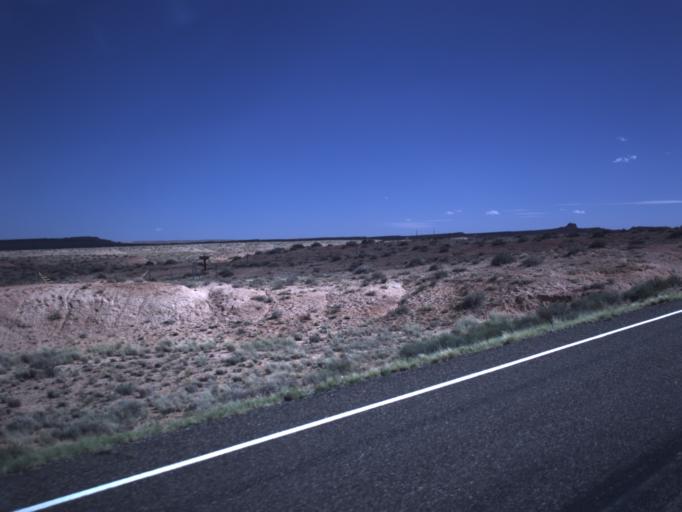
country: US
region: Utah
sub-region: Emery County
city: Ferron
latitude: 38.3028
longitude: -110.6697
